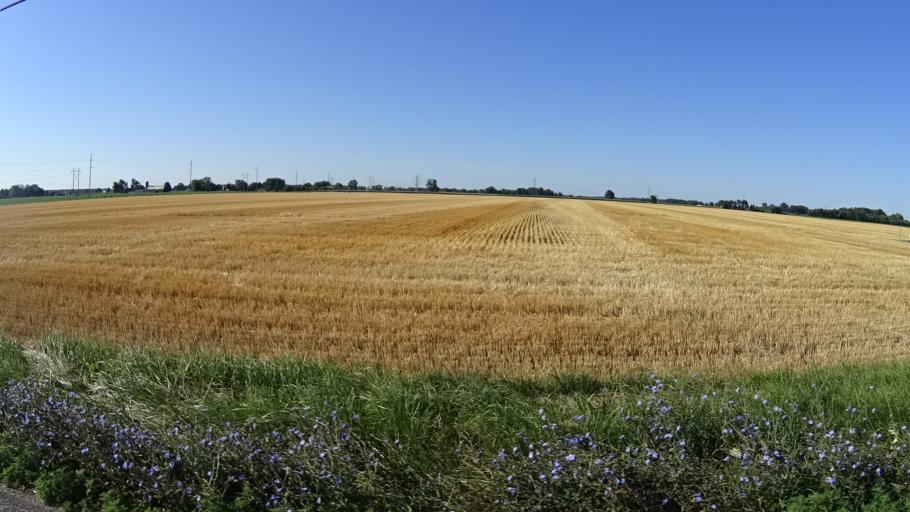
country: US
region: Ohio
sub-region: Erie County
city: Sandusky
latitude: 41.3973
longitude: -82.7420
